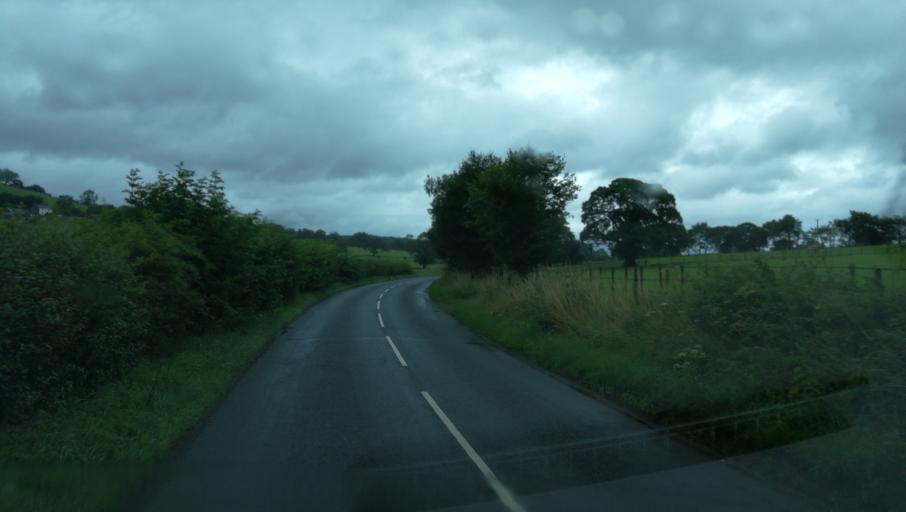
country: GB
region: England
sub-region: Cumbria
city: Penrith
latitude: 54.6150
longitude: -2.8303
